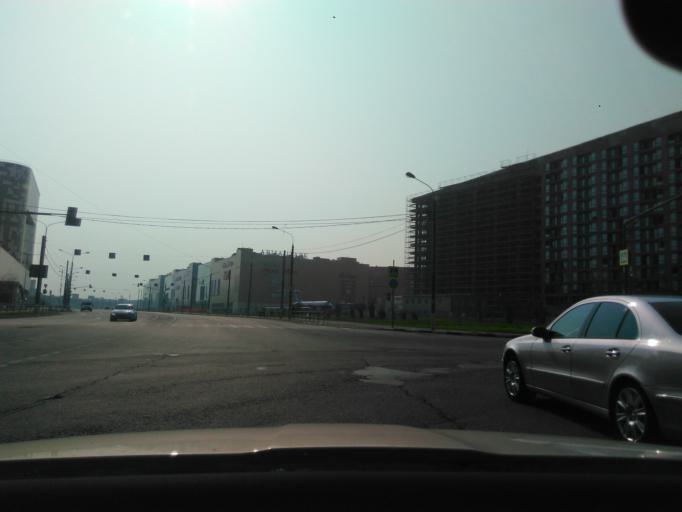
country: RU
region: Moscow
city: Sokol
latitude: 55.7926
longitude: 37.5233
